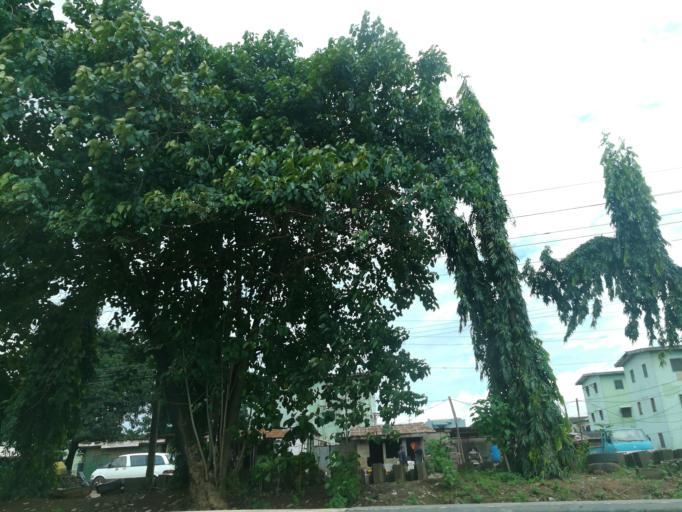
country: NG
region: Lagos
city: Ikorodu
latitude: 6.6314
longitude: 3.5092
